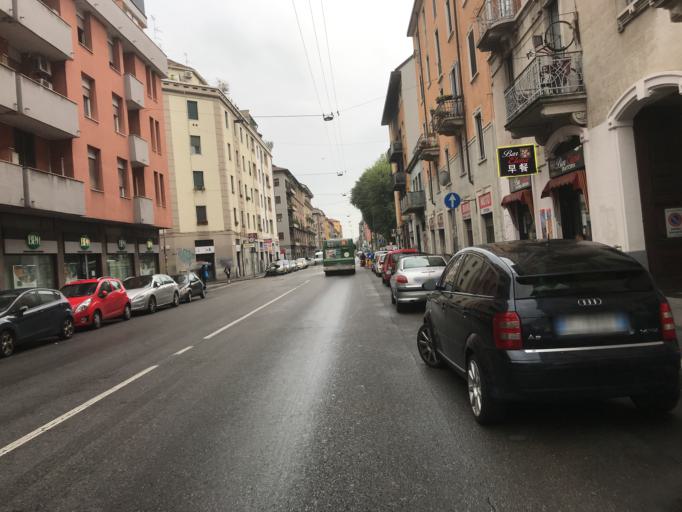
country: IT
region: Lombardy
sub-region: Citta metropolitana di Milano
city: Sesto San Giovanni
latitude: 45.4944
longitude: 9.2275
